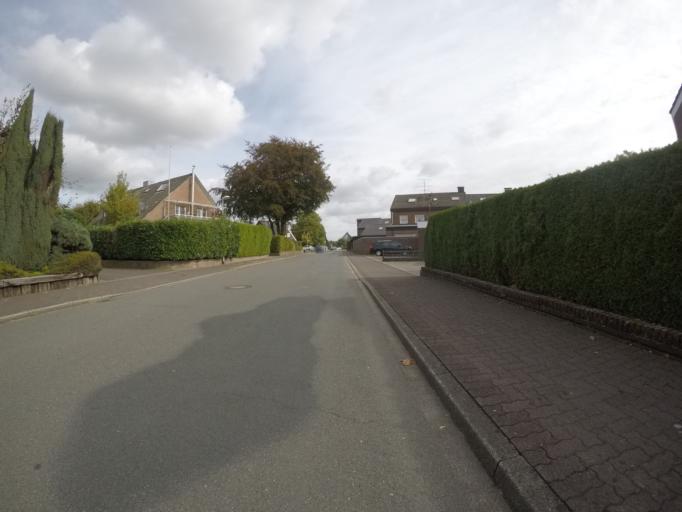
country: DE
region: North Rhine-Westphalia
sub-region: Regierungsbezirk Dusseldorf
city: Bocholt
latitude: 51.8371
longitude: 6.5782
